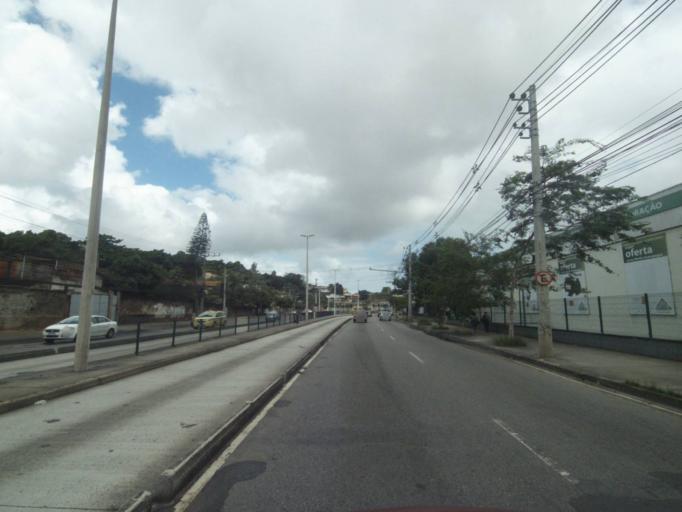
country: BR
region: Rio de Janeiro
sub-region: Sao Joao De Meriti
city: Sao Joao de Meriti
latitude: -22.9135
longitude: -43.3606
